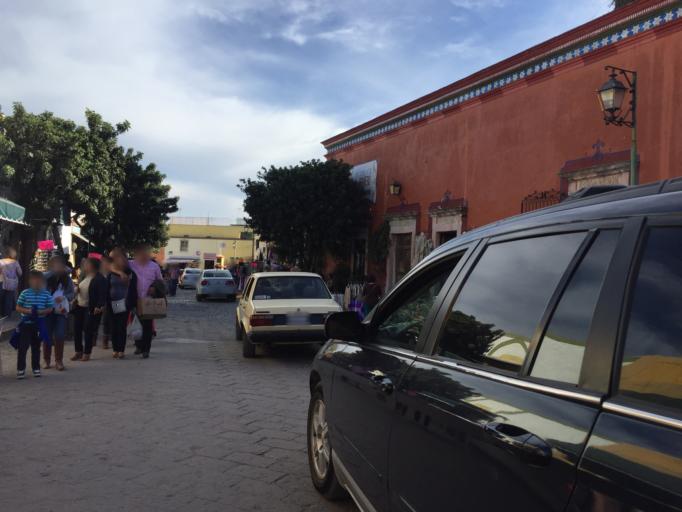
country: MX
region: Queretaro
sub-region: Ezequiel Montes
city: San Jose del Jagueey
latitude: 20.7397
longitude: -99.9411
